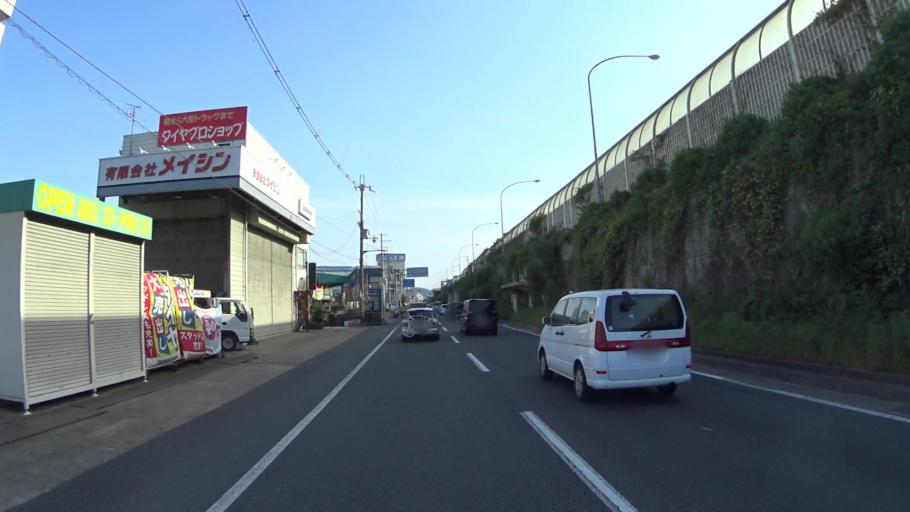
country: JP
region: Kyoto
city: Muko
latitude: 34.9243
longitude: 135.7152
